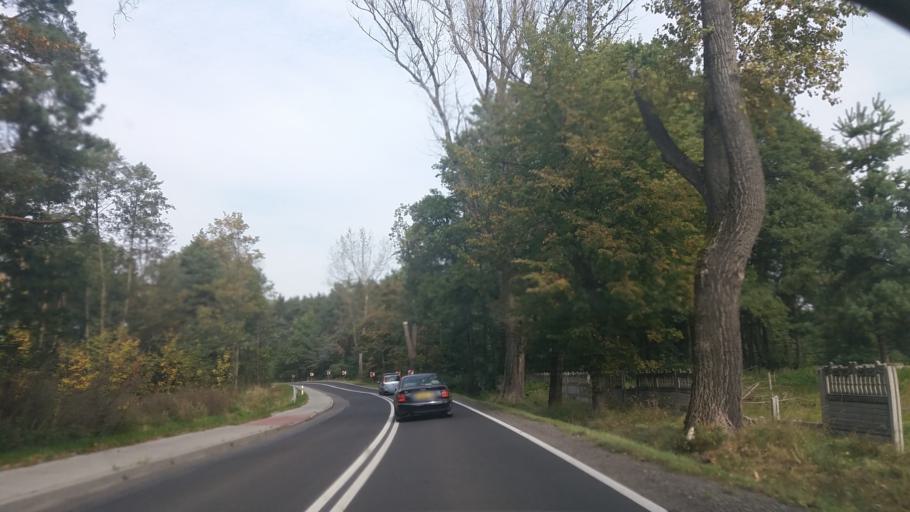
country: PL
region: Lesser Poland Voivodeship
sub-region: Powiat chrzanowski
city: Babice
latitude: 50.0579
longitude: 19.4538
